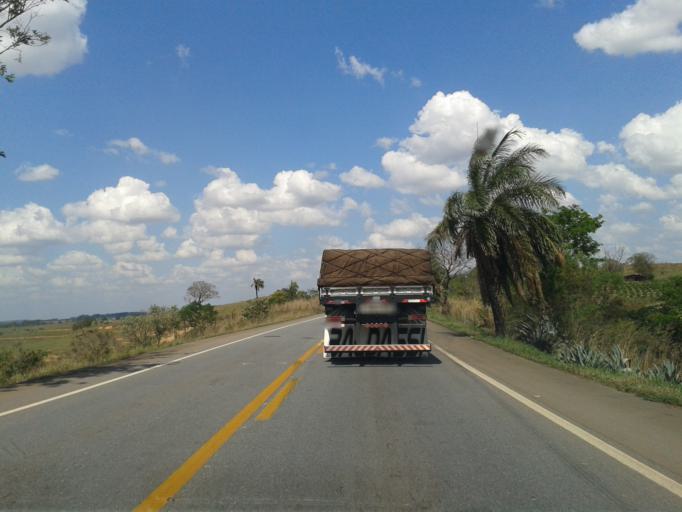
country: BR
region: Minas Gerais
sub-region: Luz
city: Luz
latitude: -19.7437
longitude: -45.8375
